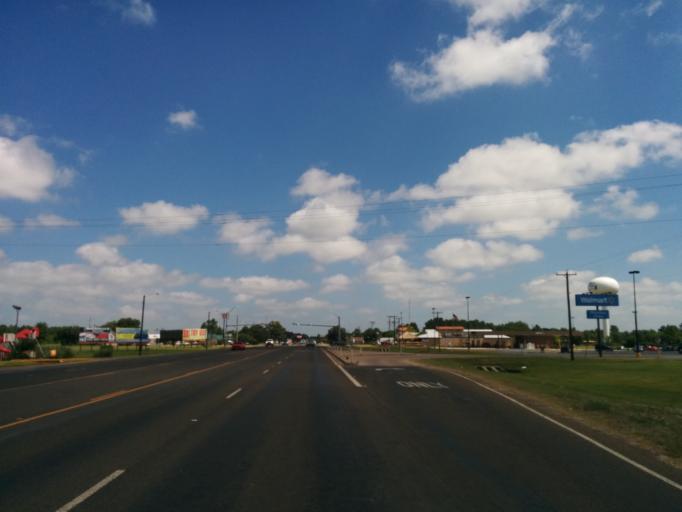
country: US
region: Texas
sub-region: Houston County
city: Crockett
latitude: 31.3186
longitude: -95.4367
